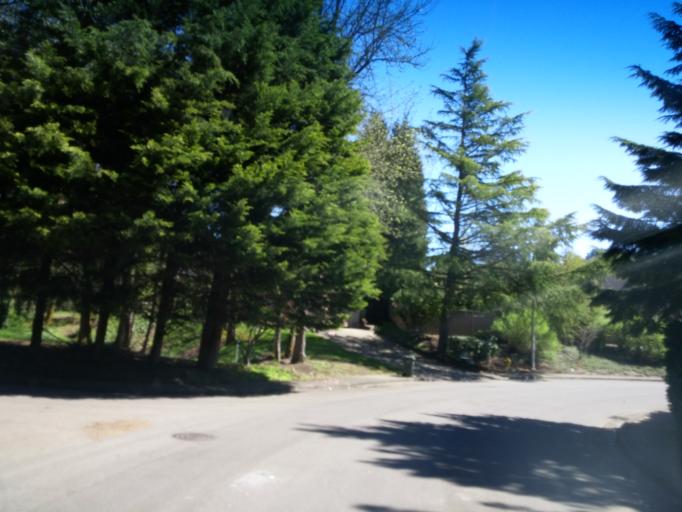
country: US
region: Oregon
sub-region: Washington County
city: West Haven
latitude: 45.5221
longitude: -122.7744
